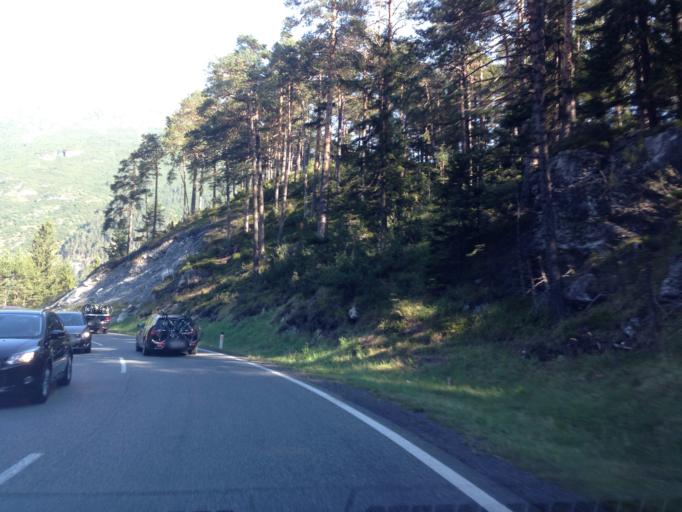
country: AT
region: Tyrol
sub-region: Politischer Bezirk Imst
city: Nassereith
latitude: 47.3583
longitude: 10.8552
